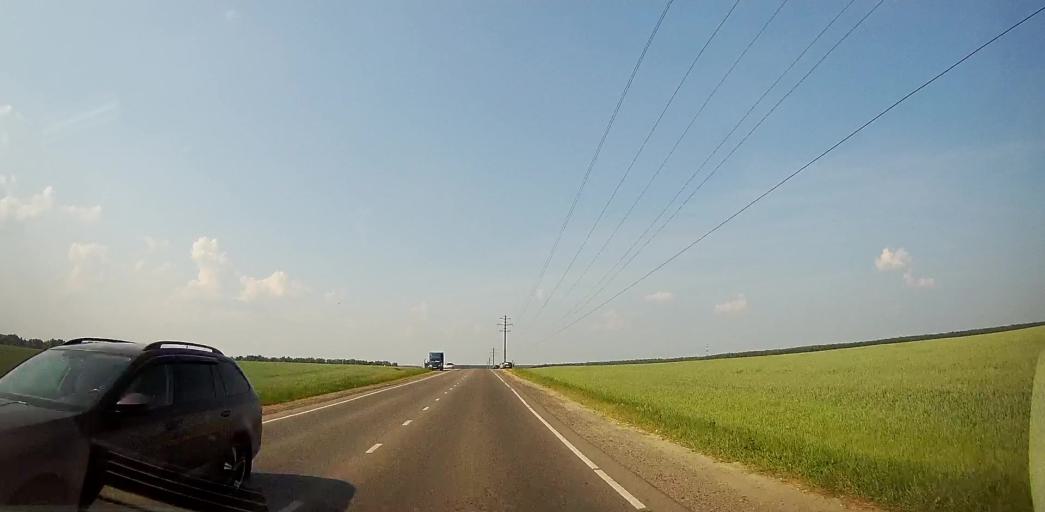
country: RU
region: Moskovskaya
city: Barybino
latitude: 55.2536
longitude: 37.9186
